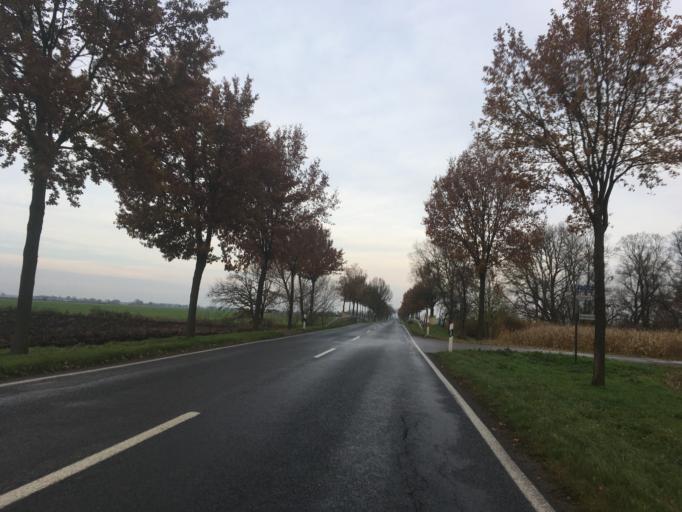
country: DE
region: Brandenburg
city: Letschin
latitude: 52.6016
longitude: 14.3502
